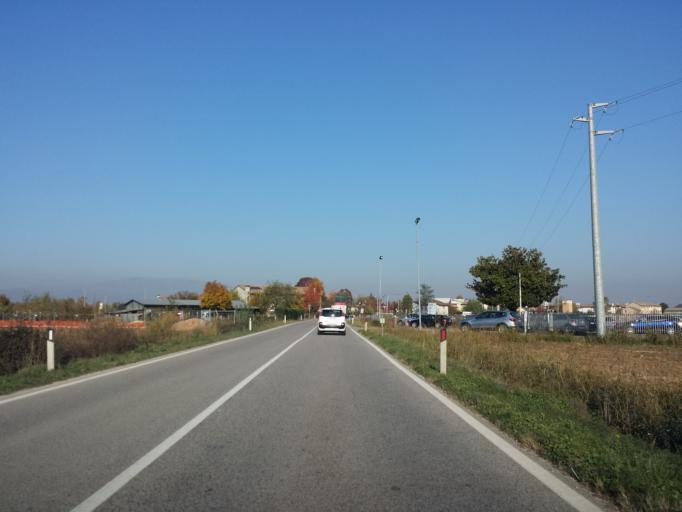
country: IT
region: Veneto
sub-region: Provincia di Treviso
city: Altivole
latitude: 45.7320
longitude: 11.9581
